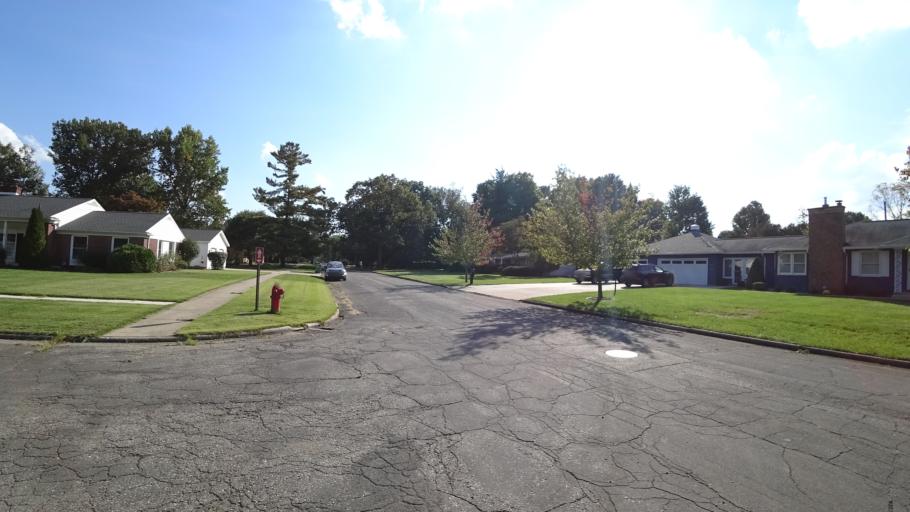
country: US
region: Michigan
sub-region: Saint Joseph County
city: Three Rivers
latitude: 41.9575
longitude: -85.6332
